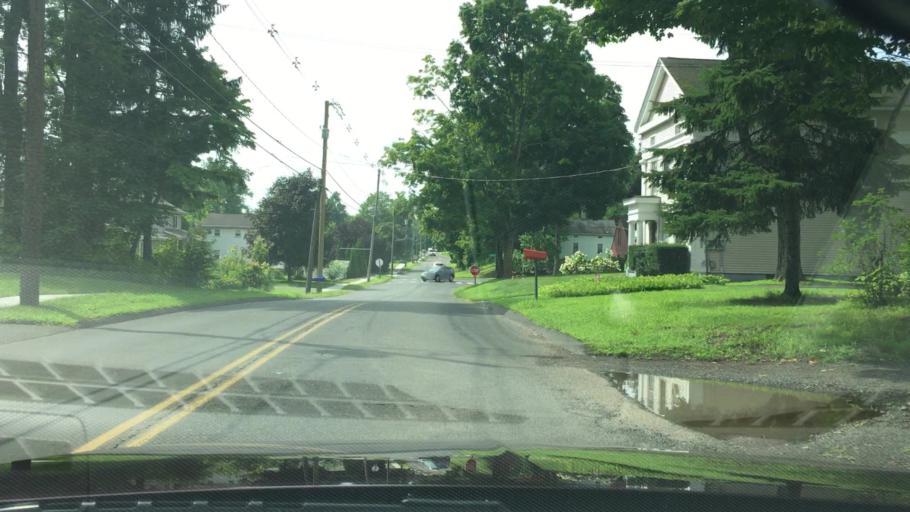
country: US
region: Connecticut
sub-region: Hartford County
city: Kensington
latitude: 41.6302
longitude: -72.7680
